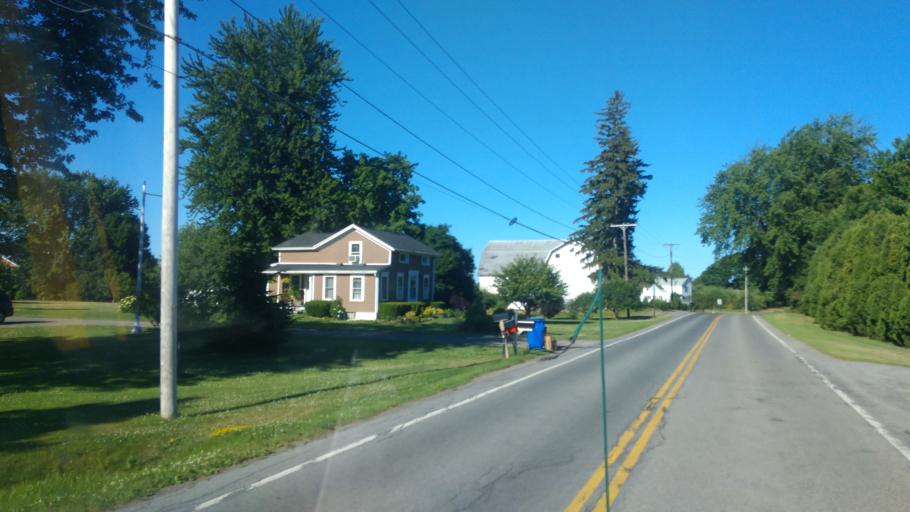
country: US
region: New York
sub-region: Wayne County
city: Williamson
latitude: 43.2806
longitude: -77.1650
